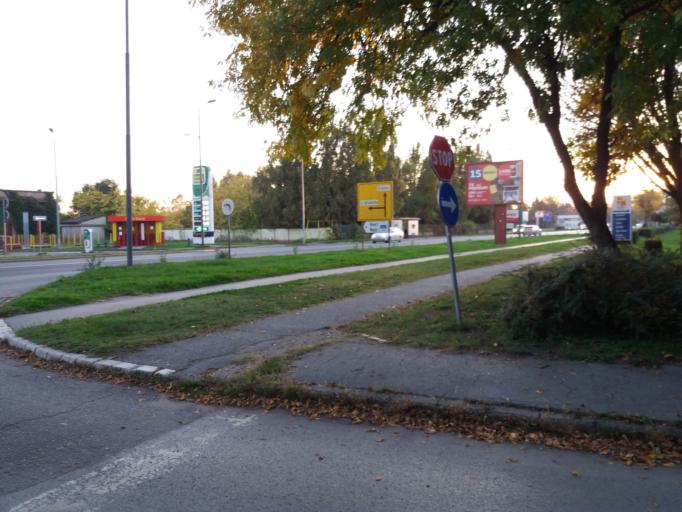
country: RS
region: Autonomna Pokrajina Vojvodina
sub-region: Severnobacki Okrug
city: Subotica
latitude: 46.1005
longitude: 19.6890
